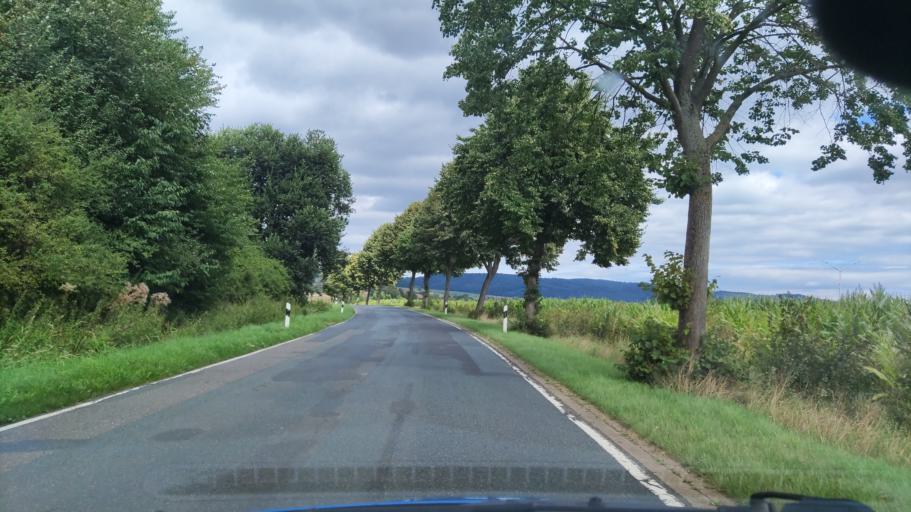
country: DE
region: Lower Saxony
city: Dassel
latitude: 51.8309
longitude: 9.7187
